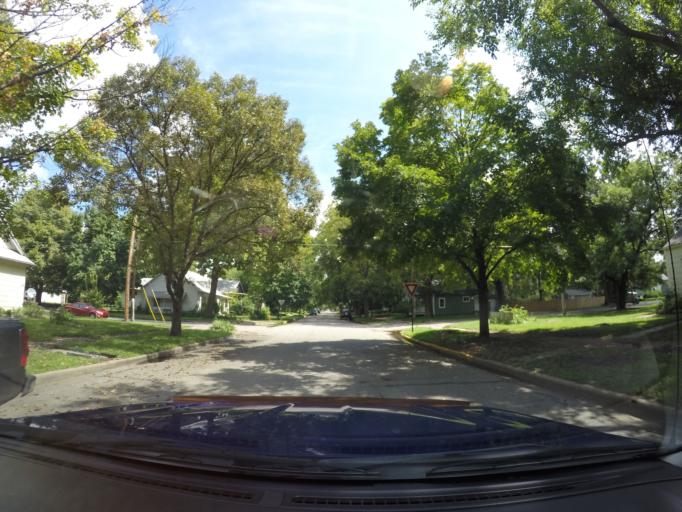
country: US
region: Kansas
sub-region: Riley County
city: Manhattan
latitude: 39.1763
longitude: -96.5705
